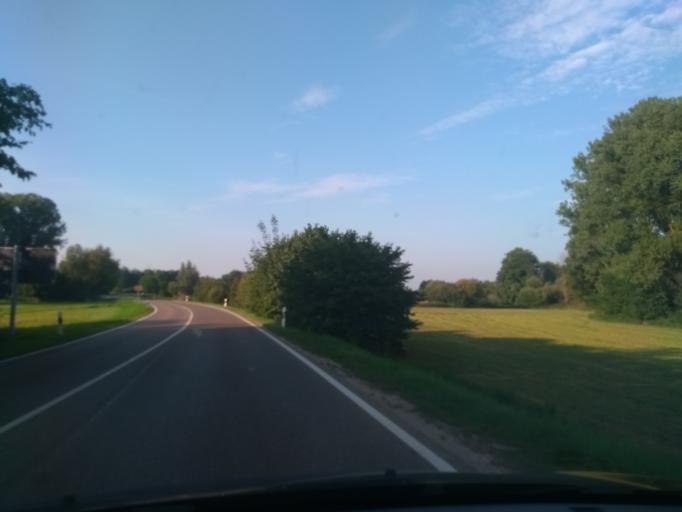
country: DE
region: Bavaria
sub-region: Upper Bavaria
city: Markt Indersdorf
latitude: 48.3607
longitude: 11.3790
